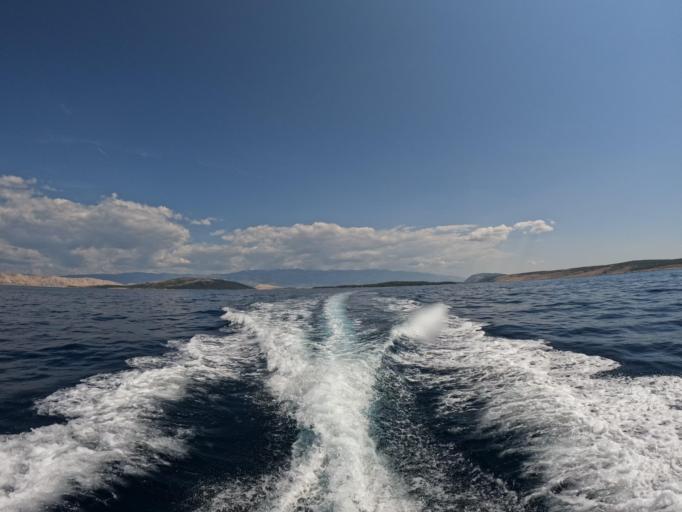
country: HR
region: Primorsko-Goranska
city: Lopar
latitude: 44.8643
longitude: 14.6874
